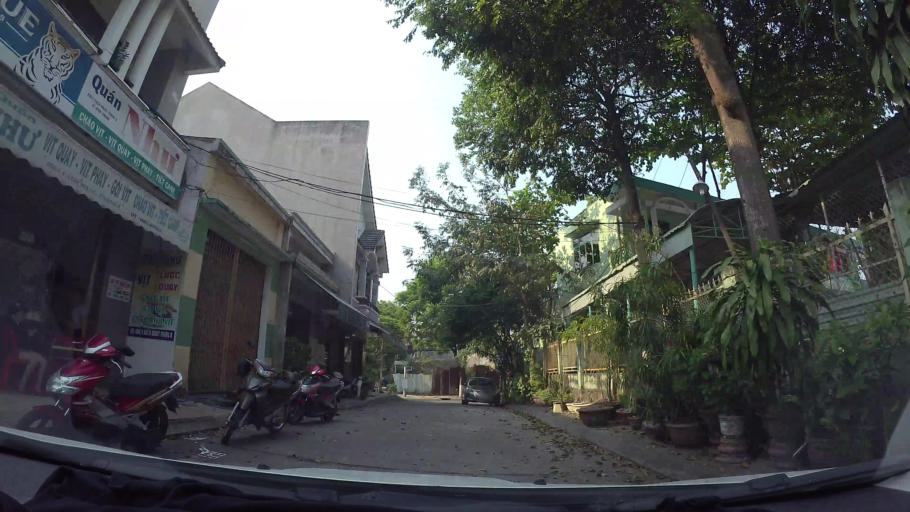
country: VN
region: Da Nang
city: Cam Le
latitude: 16.0189
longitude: 108.2078
